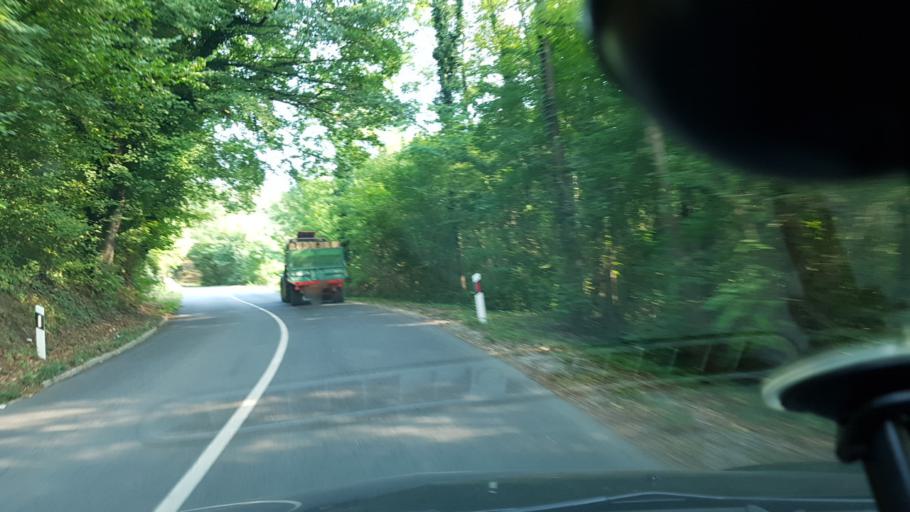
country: HR
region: Krapinsko-Zagorska
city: Pregrada
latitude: 46.1507
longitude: 15.6790
